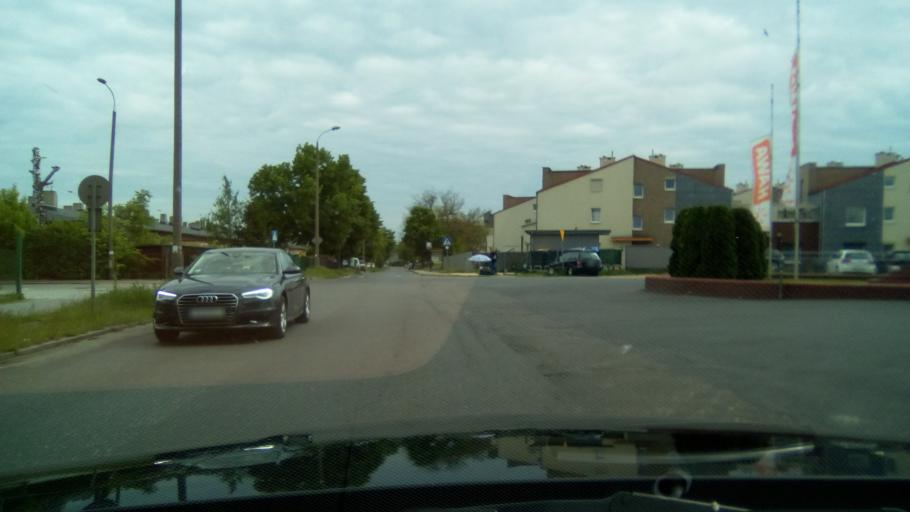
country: PL
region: Greater Poland Voivodeship
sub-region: Powiat gnieznienski
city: Gniezno
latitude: 52.5166
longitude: 17.6009
